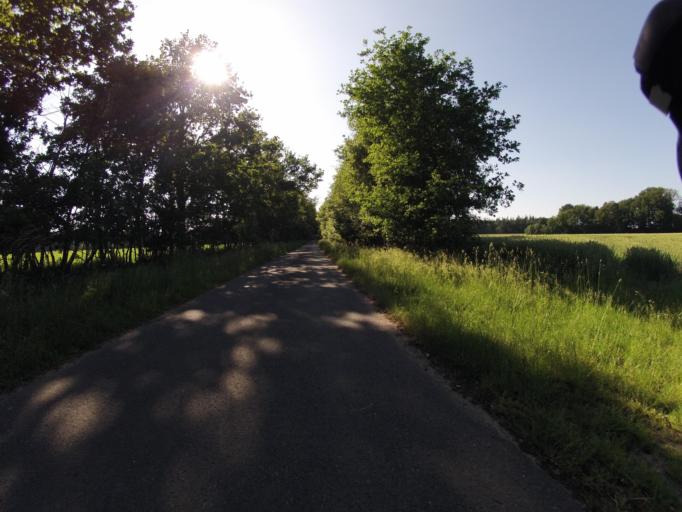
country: DE
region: Lower Saxony
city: Ohne
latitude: 52.3067
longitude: 7.3054
